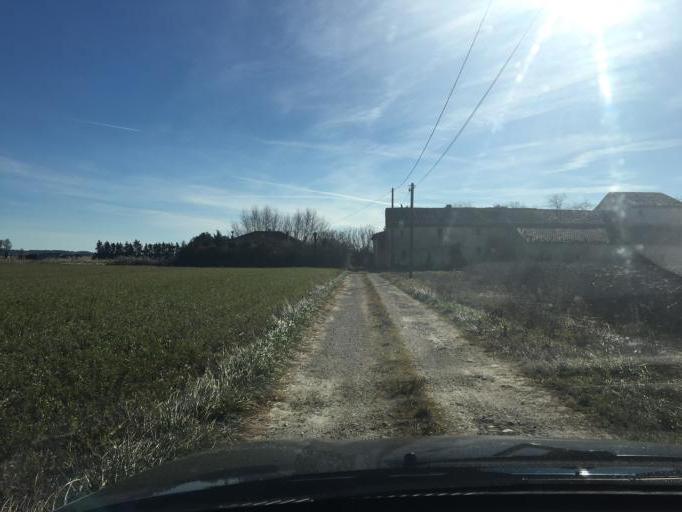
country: FR
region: Provence-Alpes-Cote d'Azur
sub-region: Departement du Vaucluse
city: Caderousse
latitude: 44.1361
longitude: 4.7611
